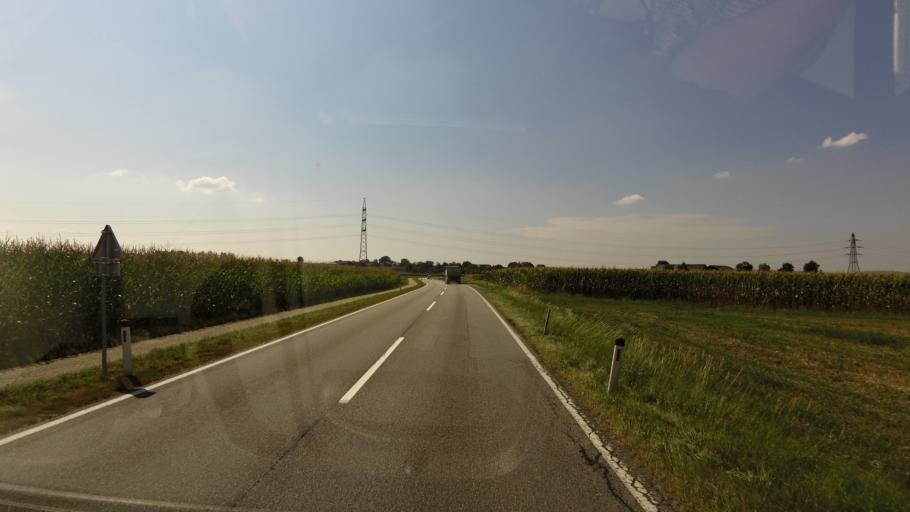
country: AT
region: Upper Austria
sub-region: Politischer Bezirk Braunau am Inn
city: Braunau am Inn
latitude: 48.2078
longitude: 13.0929
